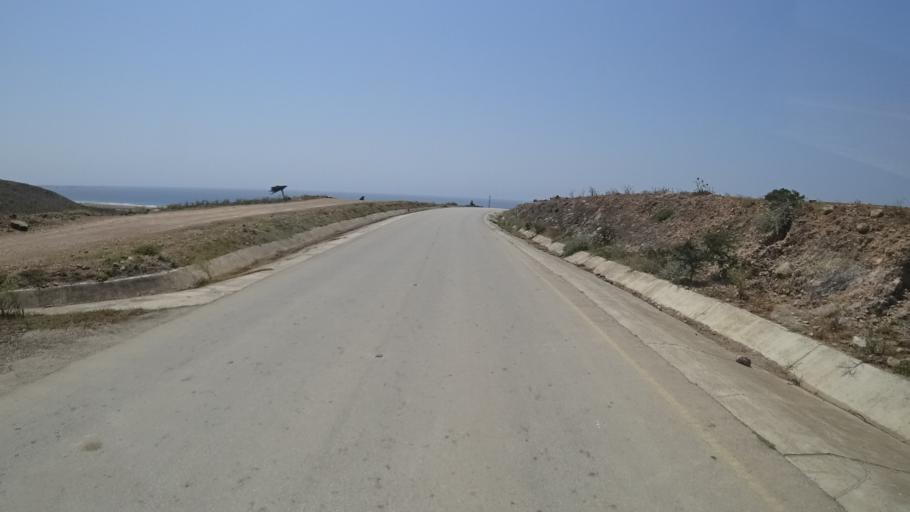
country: OM
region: Zufar
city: Salalah
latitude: 17.0411
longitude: 54.6128
